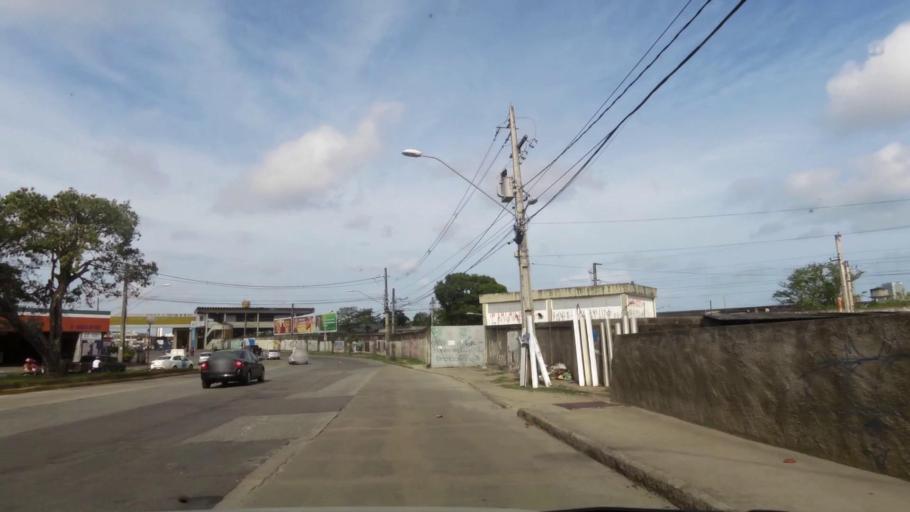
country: BR
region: Pernambuco
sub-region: Recife
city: Recife
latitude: -8.0810
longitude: -34.9049
